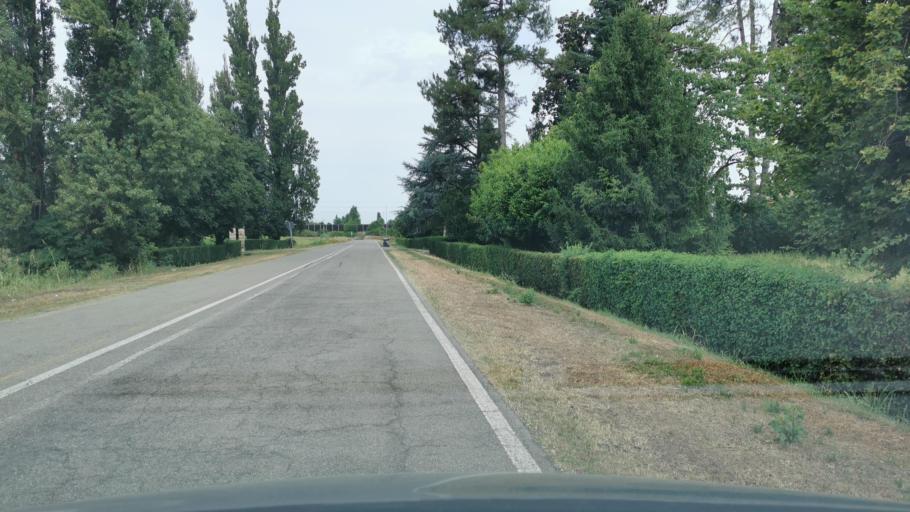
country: IT
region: Emilia-Romagna
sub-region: Provincia di Modena
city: Campogalliano
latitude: 44.6834
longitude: 10.8746
